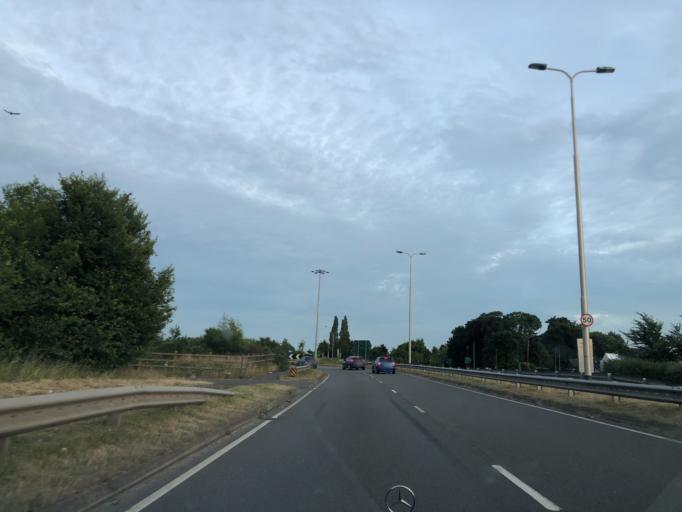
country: GB
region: England
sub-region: Solihull
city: Barston
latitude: 52.4141
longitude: -1.6748
